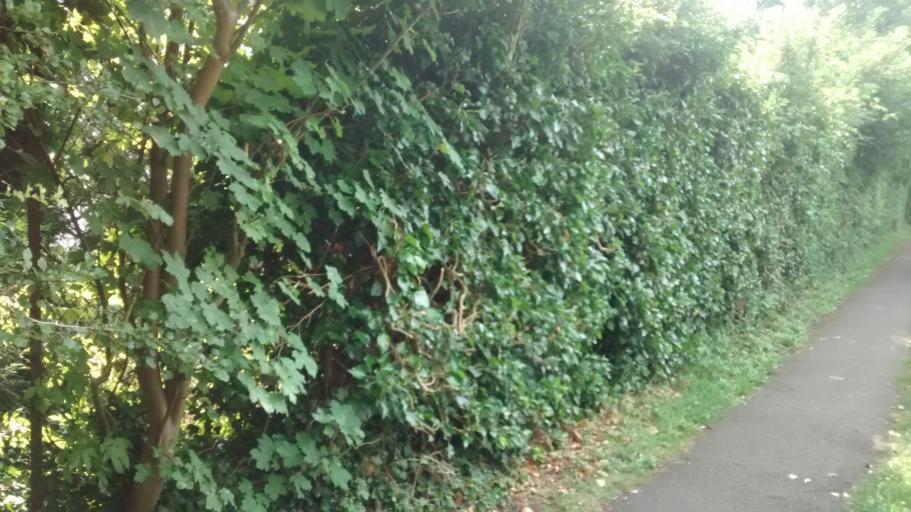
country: GB
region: England
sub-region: Cambridgeshire
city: Cambridge
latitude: 52.2019
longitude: 0.0994
